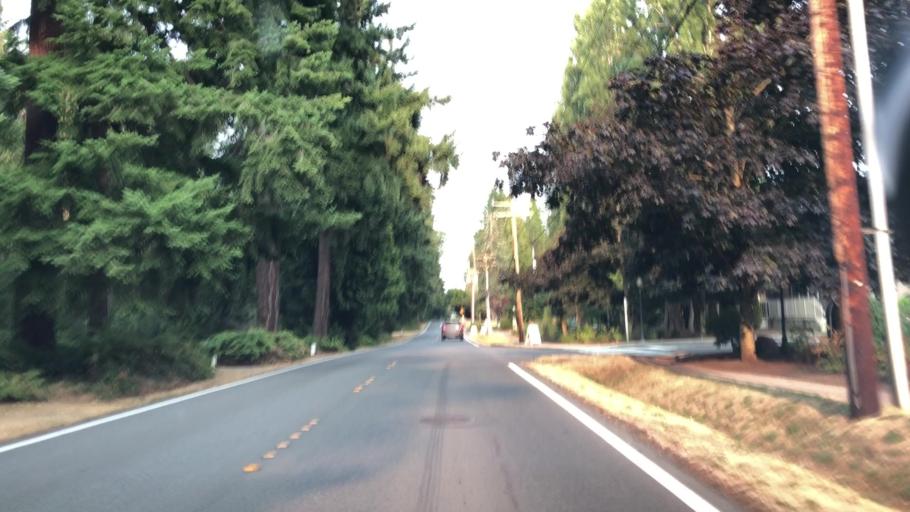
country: US
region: Washington
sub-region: King County
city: Mercer Island
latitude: 47.5420
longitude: -122.2262
